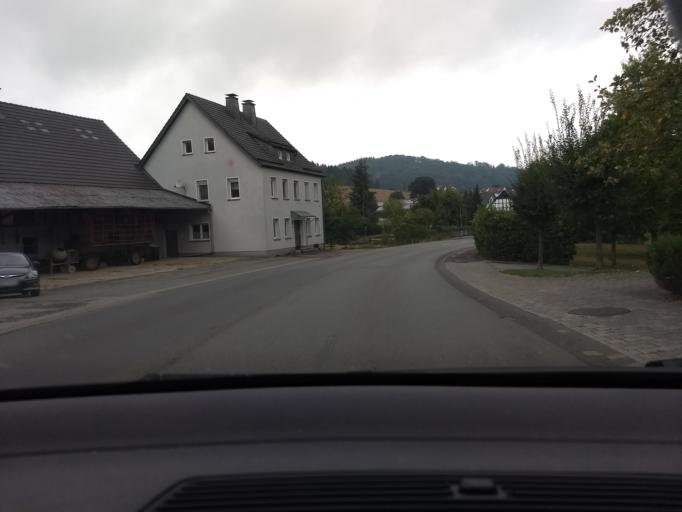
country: DE
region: North Rhine-Westphalia
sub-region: Regierungsbezirk Arnsberg
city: Arnsberg
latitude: 51.3548
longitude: 8.1655
